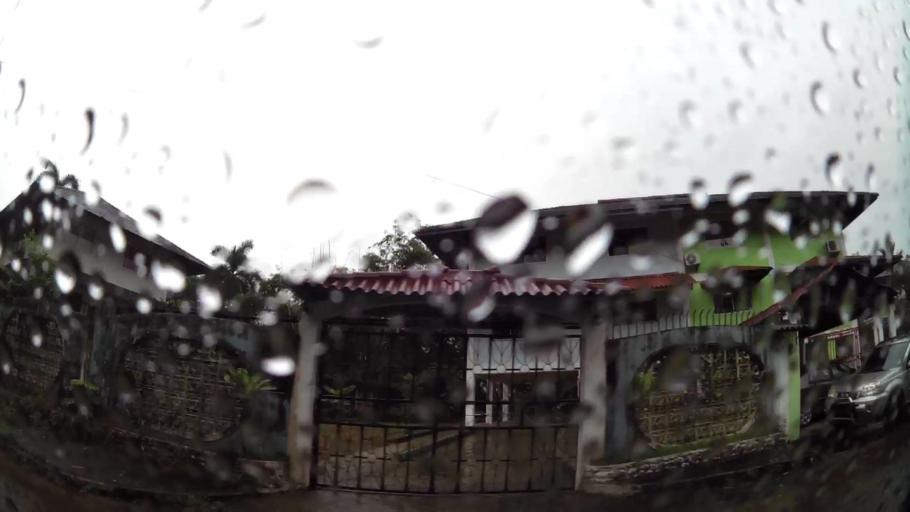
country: PA
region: Colon
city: Las Margaritas
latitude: 9.3155
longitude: -79.8700
